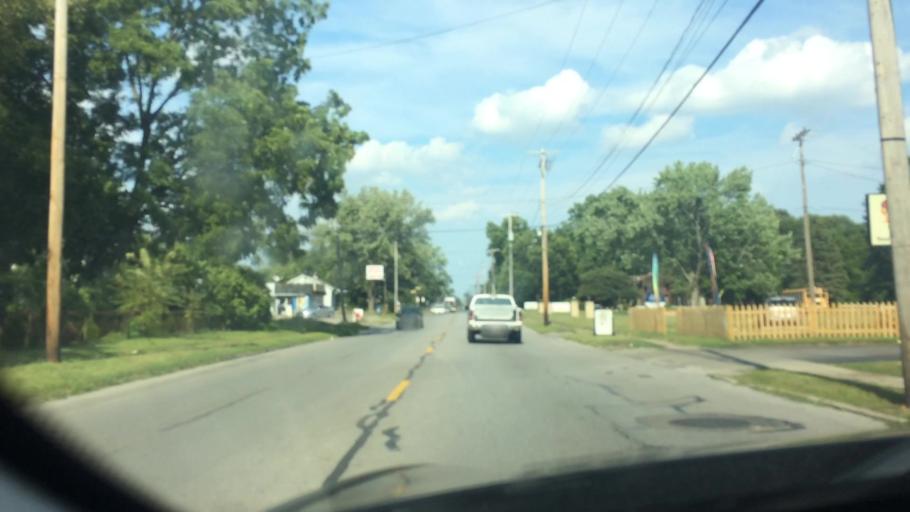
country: US
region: Ohio
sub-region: Lucas County
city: Ottawa Hills
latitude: 41.6250
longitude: -83.6225
